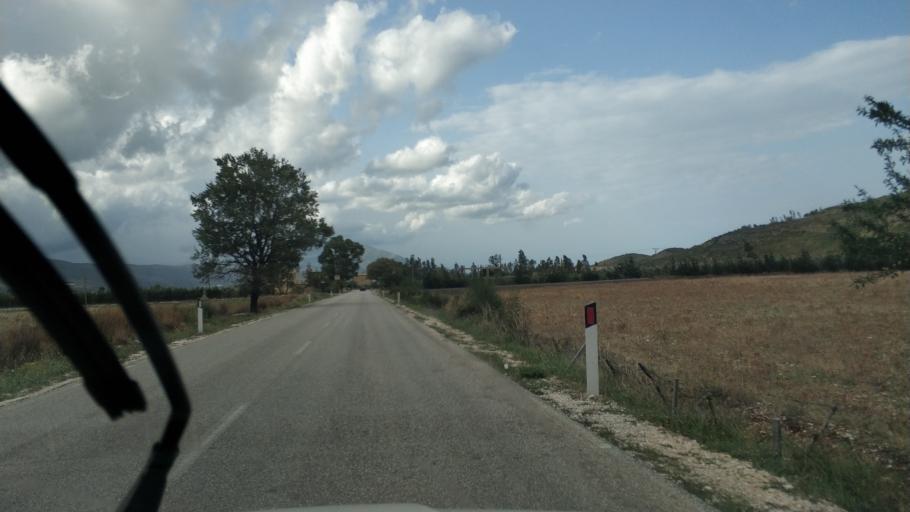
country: AL
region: Vlore
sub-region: Rrethi i Vlores
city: Orikum
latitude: 40.2769
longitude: 19.5059
